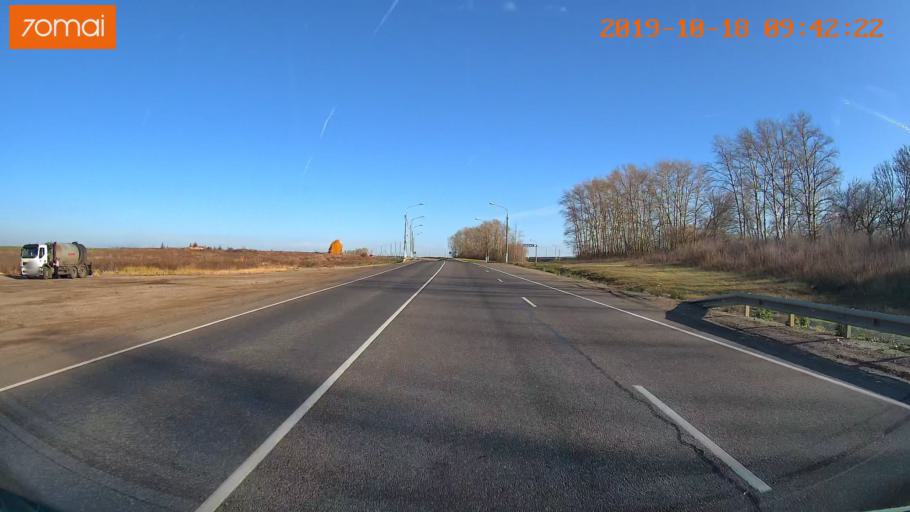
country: RU
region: Tula
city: Kazachka
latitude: 53.2862
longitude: 38.1756
